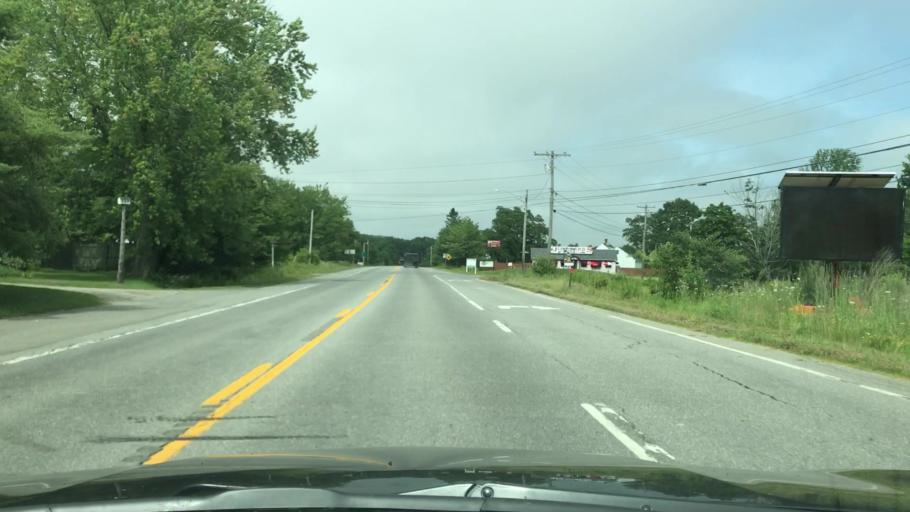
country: US
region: Maine
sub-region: Waldo County
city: Stockton Springs
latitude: 44.4852
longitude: -68.8654
